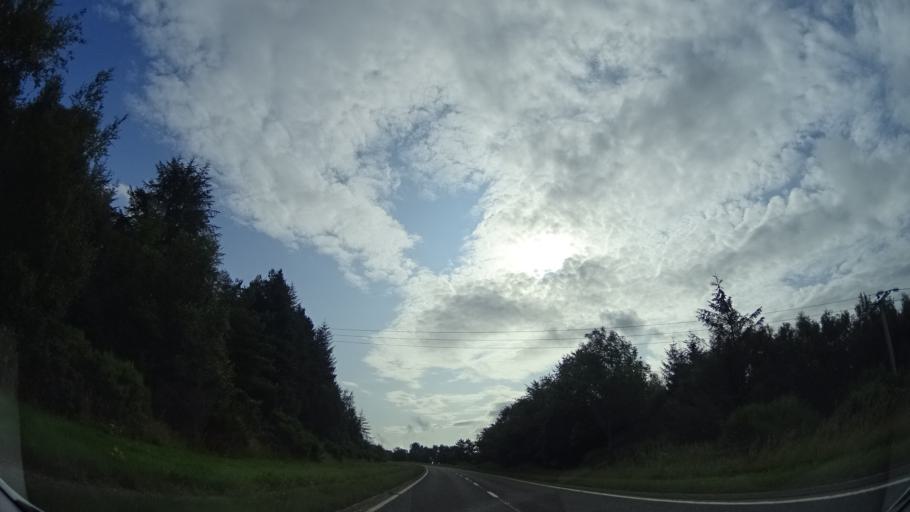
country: GB
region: Scotland
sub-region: Highland
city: Muir of Ord
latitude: 57.5582
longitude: -4.5088
